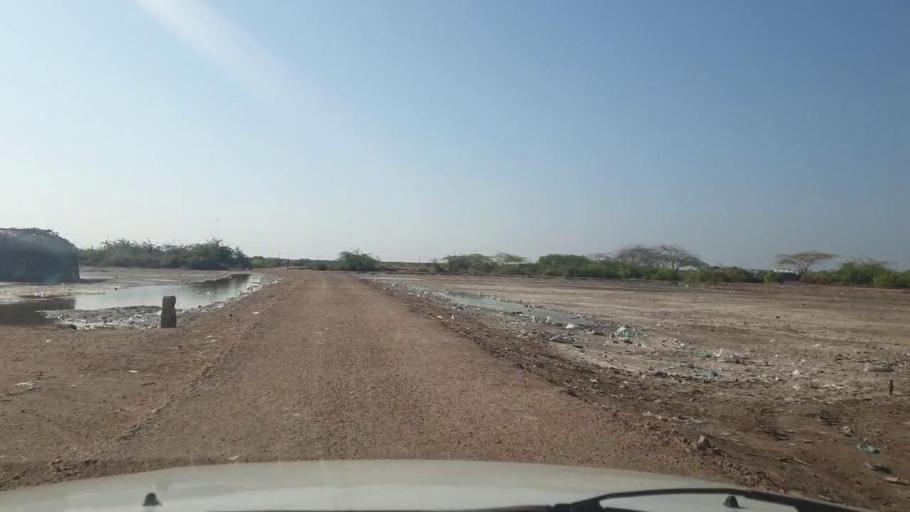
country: PK
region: Sindh
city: Chuhar Jamali
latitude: 24.4651
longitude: 67.9251
